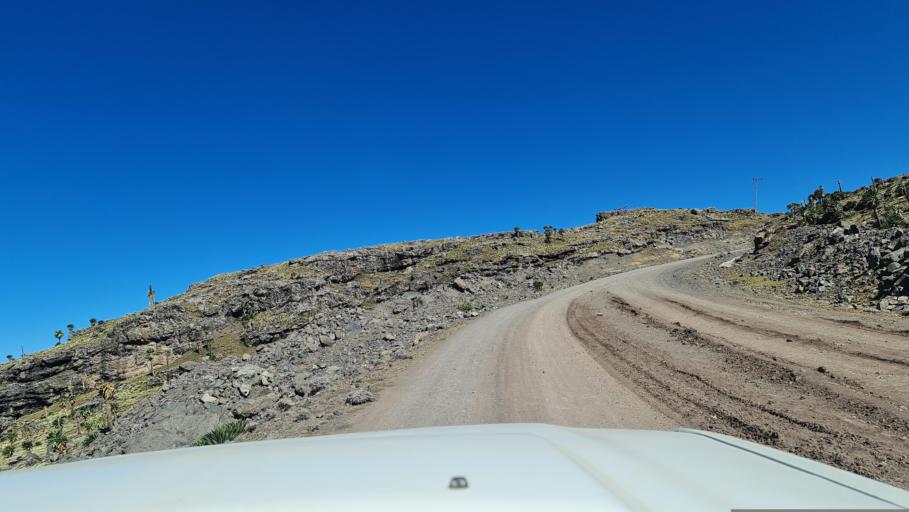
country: ET
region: Amhara
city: Debark'
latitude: 13.2222
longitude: 38.2197
